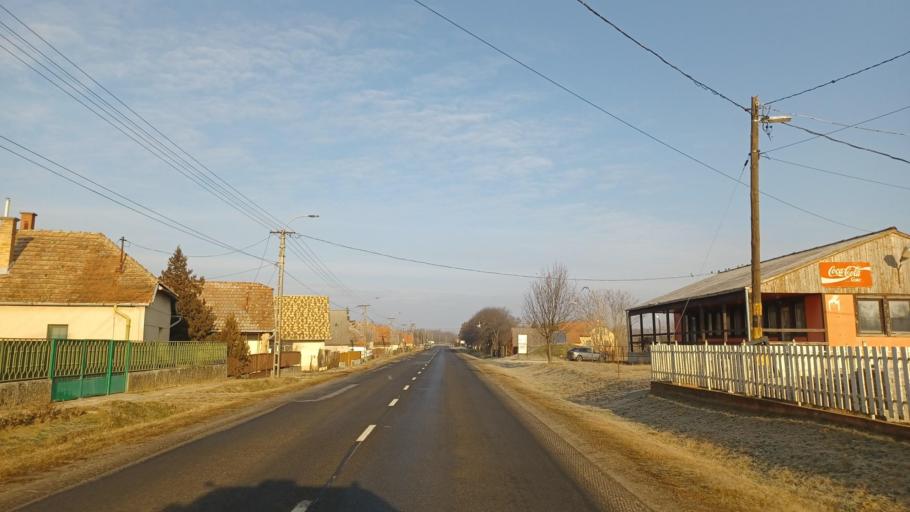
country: HU
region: Fejer
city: Cece
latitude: 46.7212
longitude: 18.6626
